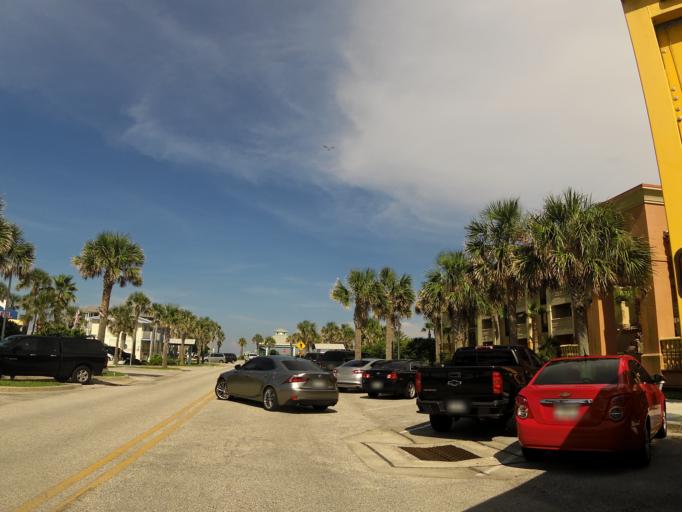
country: US
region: Florida
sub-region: Saint Johns County
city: Villano Beach
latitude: 29.9168
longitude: -81.2922
